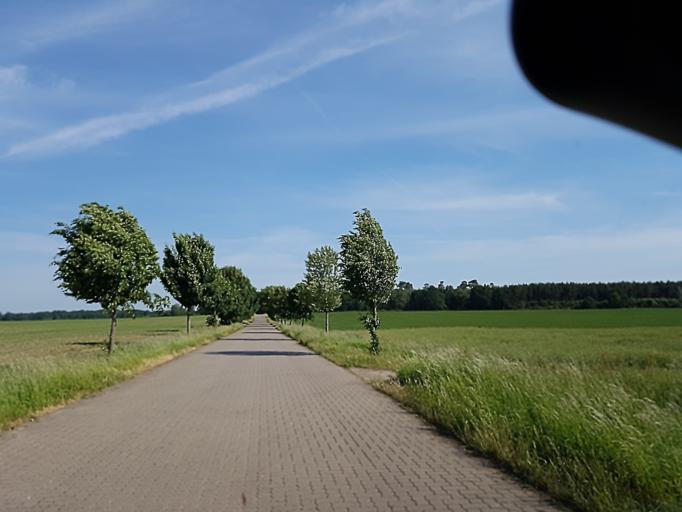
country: DE
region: Saxony-Anhalt
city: Rosslau
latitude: 52.0369
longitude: 12.2797
